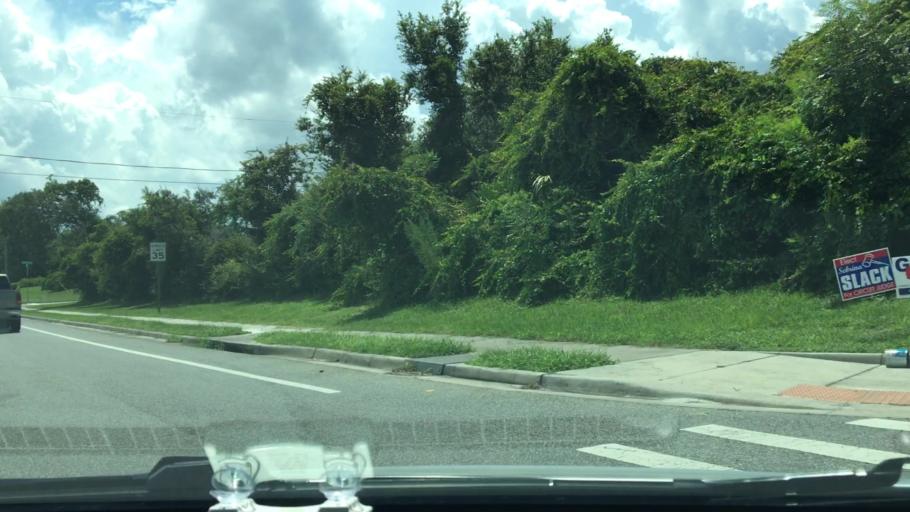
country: US
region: Florida
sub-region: Volusia County
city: Deltona
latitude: 28.8910
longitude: -81.2170
